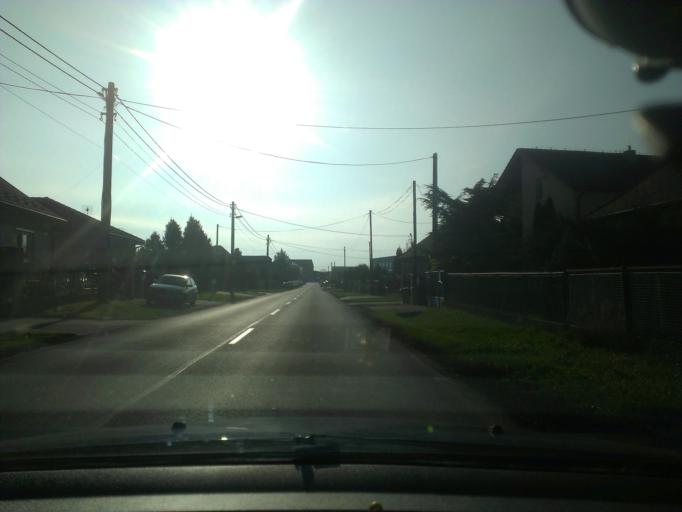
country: SK
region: Nitriansky
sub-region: Okres Nitra
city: Nitra
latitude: 48.3733
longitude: 18.0248
